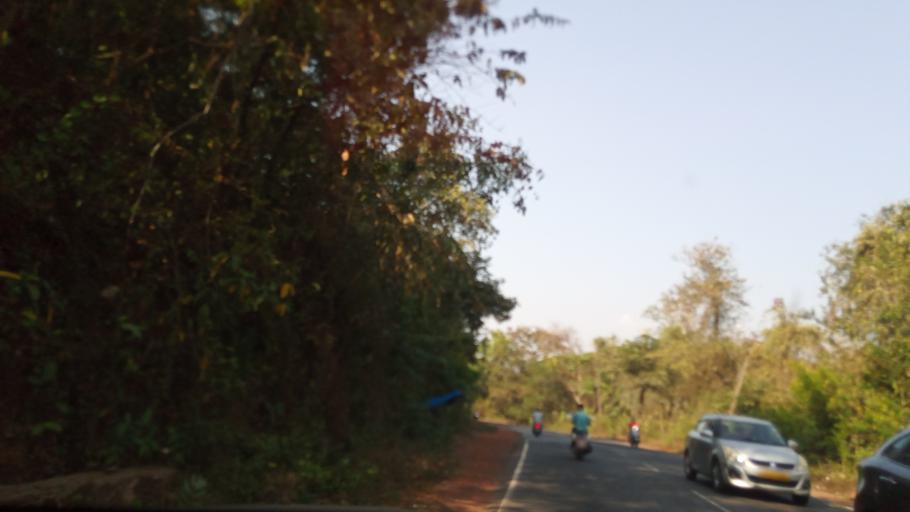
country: IN
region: Goa
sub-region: North Goa
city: Bandora
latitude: 15.4248
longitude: 73.9871
